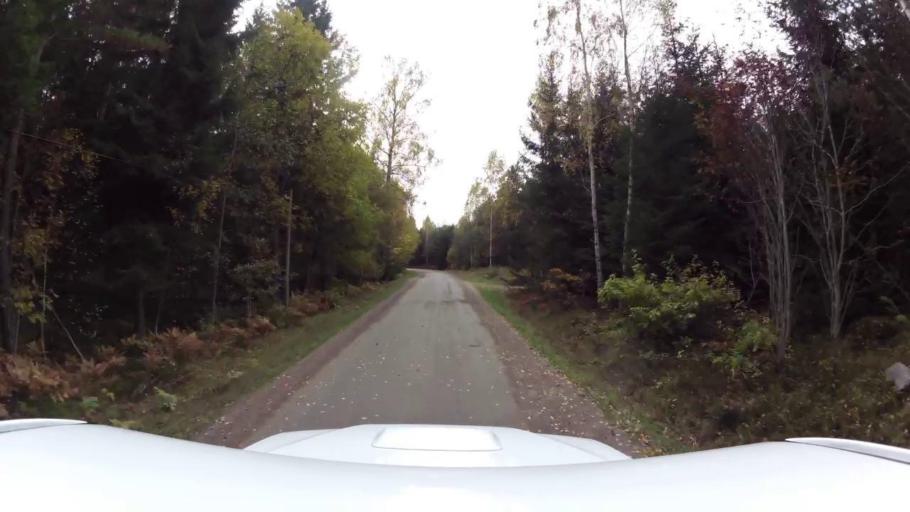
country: SE
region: OEstergoetland
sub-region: Linkopings Kommun
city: Ekangen
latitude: 58.5531
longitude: 15.6625
